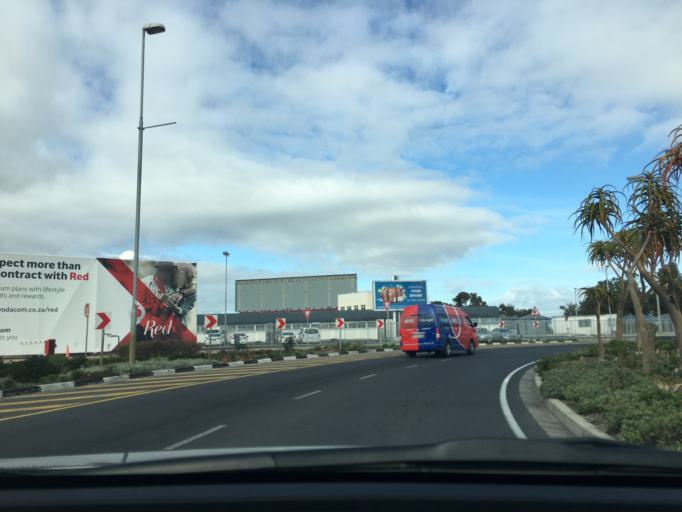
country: ZA
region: Western Cape
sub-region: City of Cape Town
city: Lansdowne
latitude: -33.9723
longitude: 18.5963
